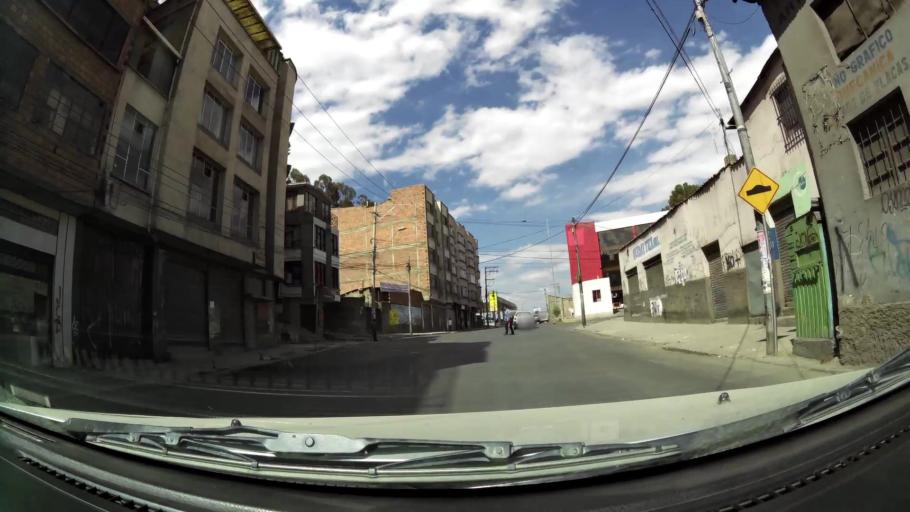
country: BO
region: La Paz
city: La Paz
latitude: -16.4958
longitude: -68.1291
